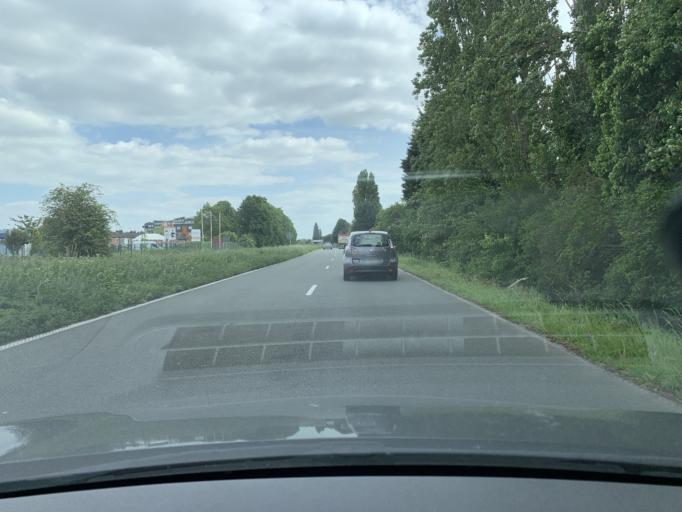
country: FR
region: Nord-Pas-de-Calais
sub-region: Departement du Nord
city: Cuincy
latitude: 50.3812
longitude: 3.0560
